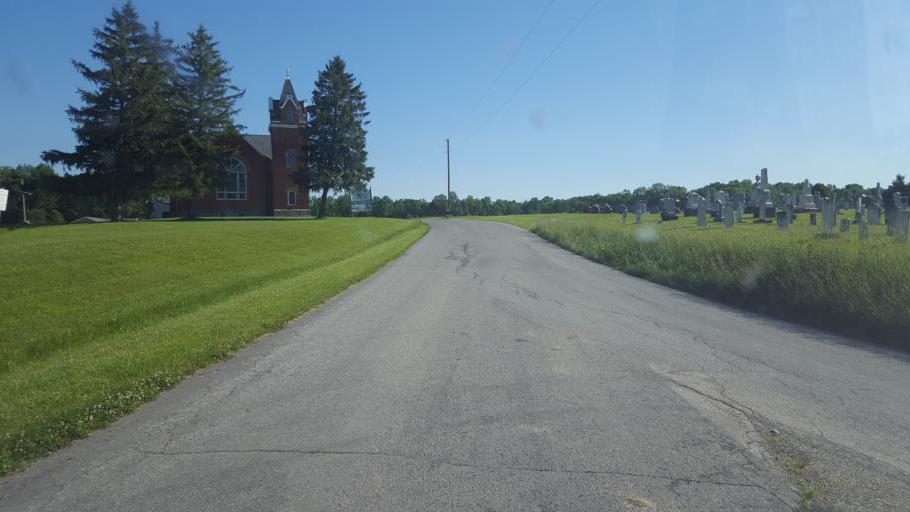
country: US
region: Ohio
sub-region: Crawford County
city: Bucyrus
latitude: 40.7432
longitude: -82.9154
